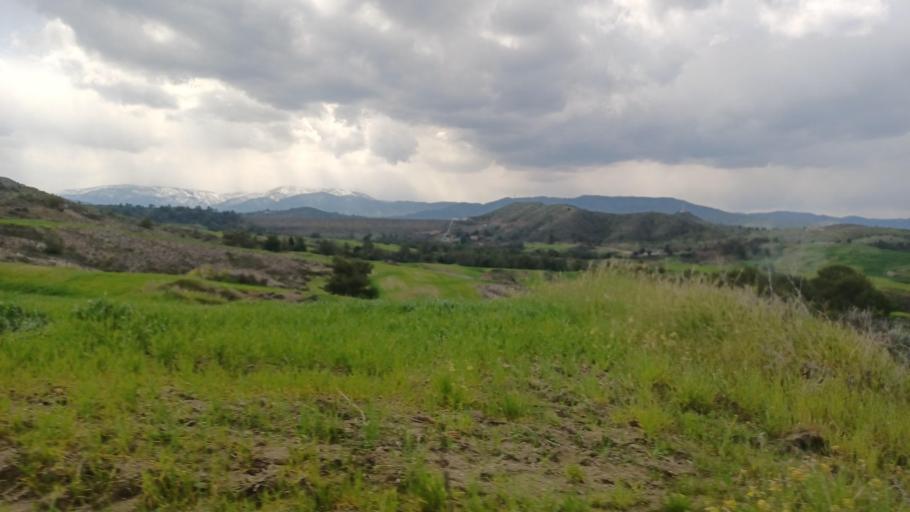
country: CY
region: Lefkosia
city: Lefka
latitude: 35.0805
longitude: 32.9081
